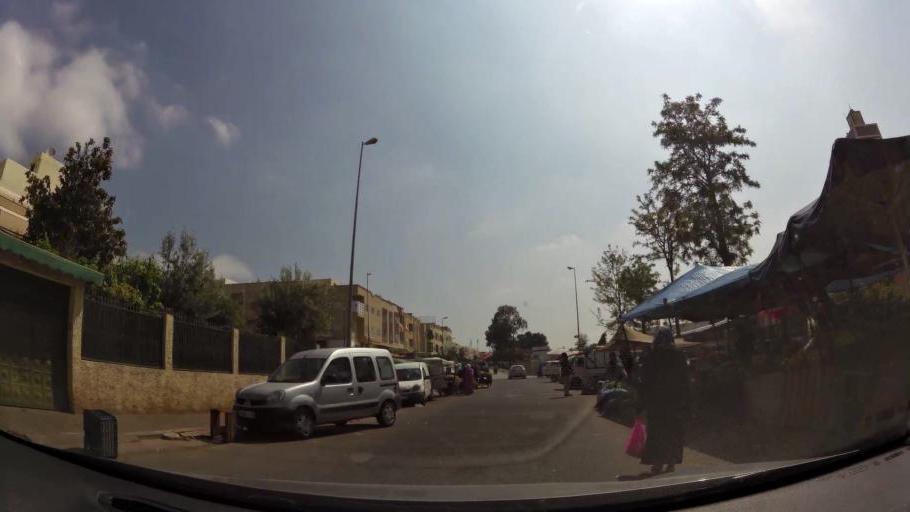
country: MA
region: Fes-Boulemane
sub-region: Fes
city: Fes
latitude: 34.0584
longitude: -5.0216
